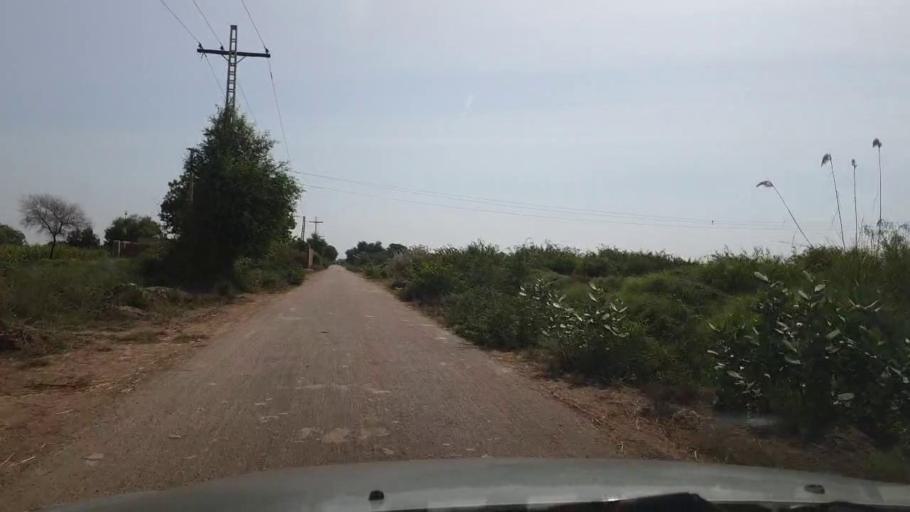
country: PK
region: Sindh
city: Tando Muhammad Khan
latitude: 25.1512
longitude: 68.3885
